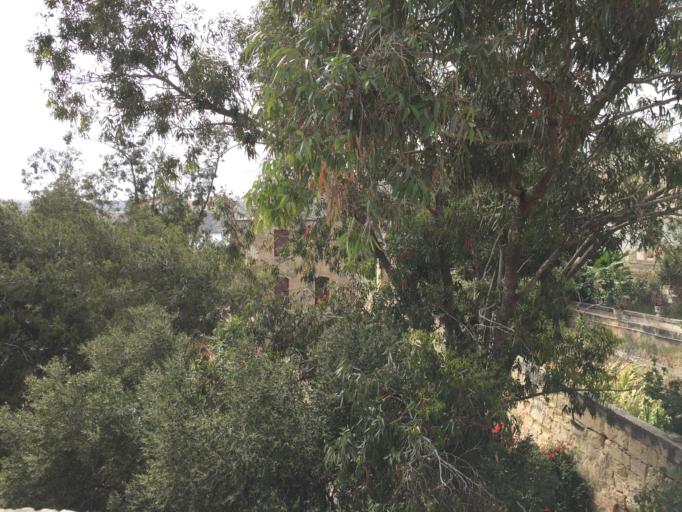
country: MT
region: Bormla
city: Cospicua
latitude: 35.8903
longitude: 14.5262
